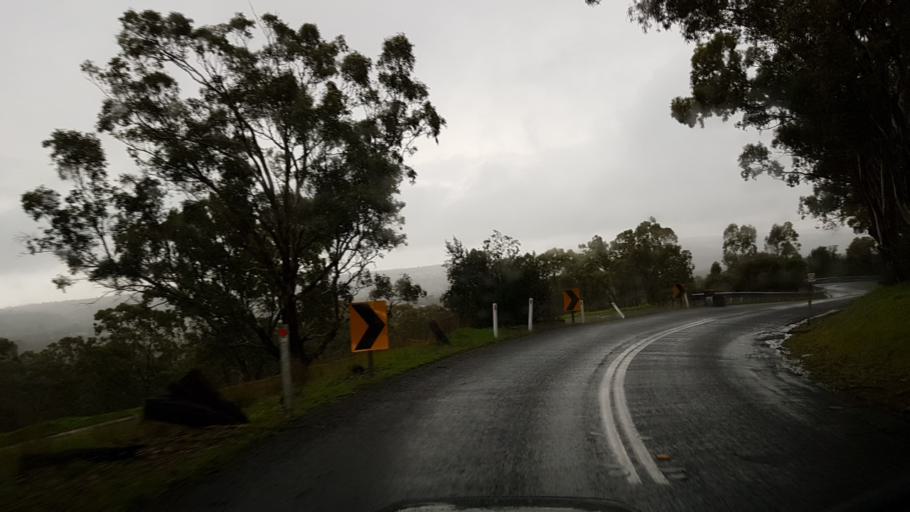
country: AU
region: South Australia
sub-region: Onkaparinga
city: Craigburn Farm
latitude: -35.0660
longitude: 138.6218
